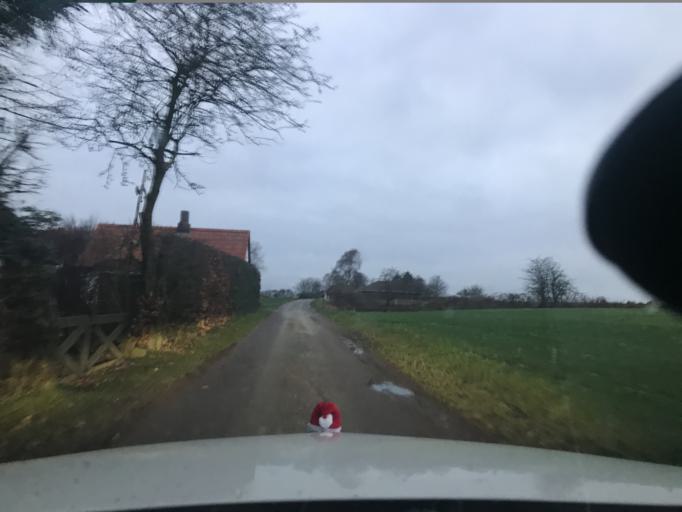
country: DK
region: South Denmark
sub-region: Sonderborg Kommune
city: Dybbol
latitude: 54.8472
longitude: 9.7438
